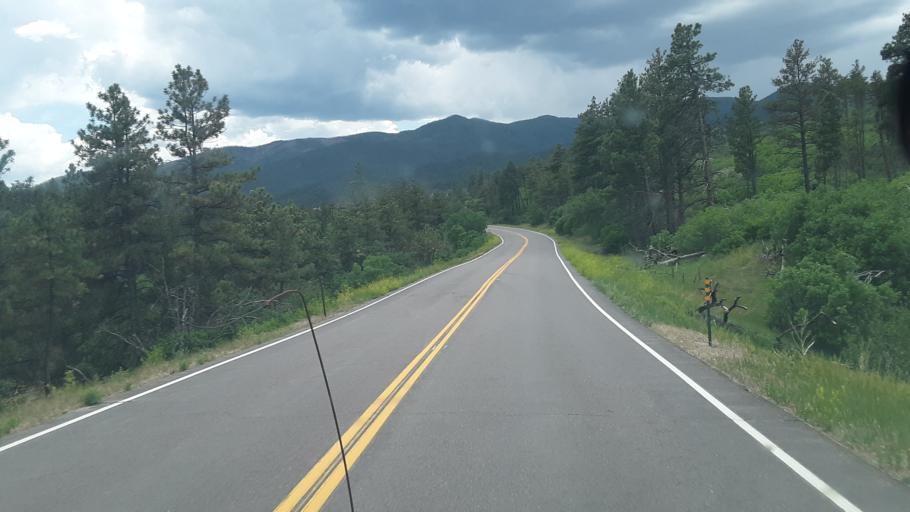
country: US
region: Colorado
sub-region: Fremont County
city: Florence
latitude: 38.1941
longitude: -105.1038
